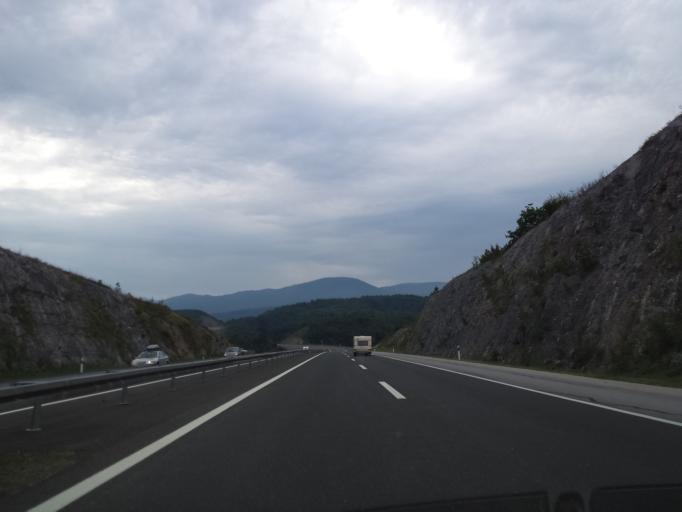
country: HR
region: Karlovacka
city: Ostarije
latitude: 45.1592
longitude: 15.2729
